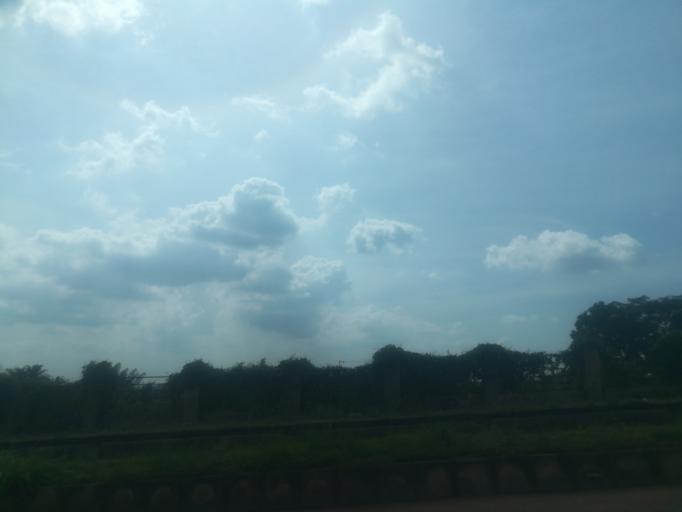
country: NG
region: Ogun
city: Abeokuta
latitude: 7.1737
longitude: 3.3831
